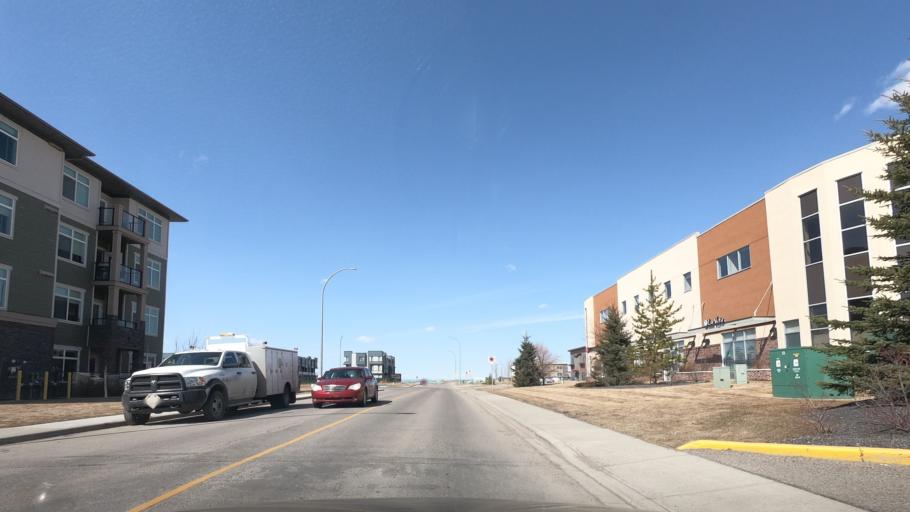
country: CA
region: Alberta
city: Airdrie
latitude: 51.3045
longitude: -114.0112
